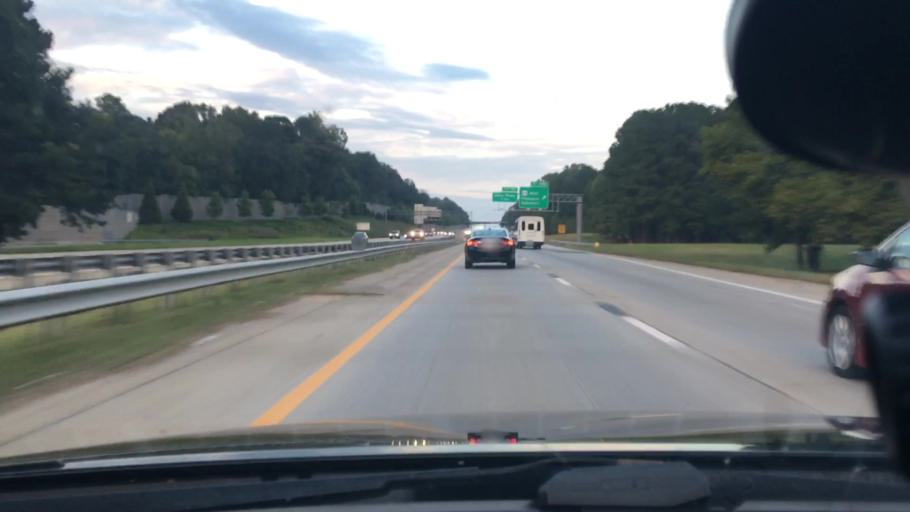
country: US
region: North Carolina
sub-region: Wake County
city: Cary
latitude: 35.7378
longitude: -78.7919
